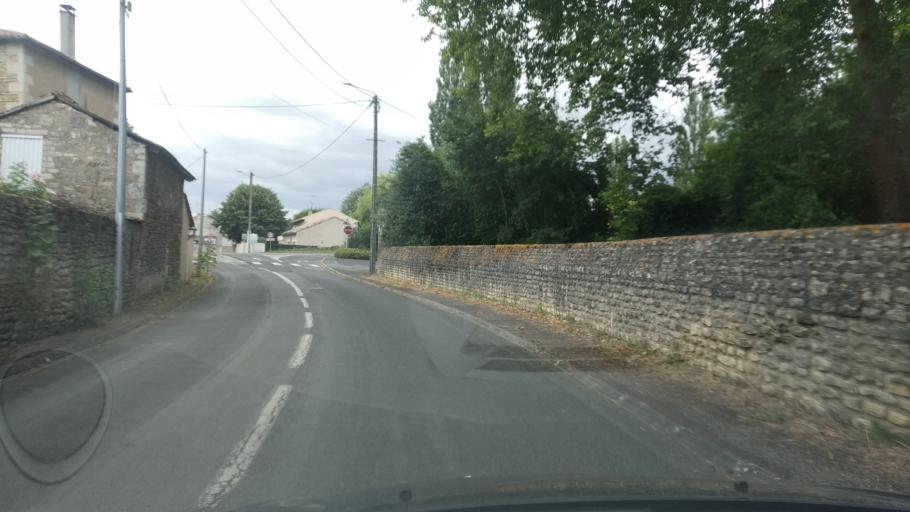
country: FR
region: Poitou-Charentes
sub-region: Departement de la Vienne
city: Vouille
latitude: 46.6372
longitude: 0.1680
